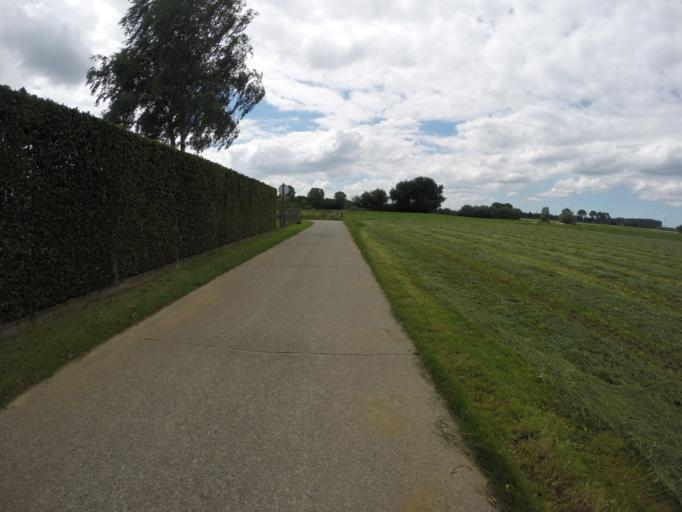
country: BE
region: Flanders
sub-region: Provincie Oost-Vlaanderen
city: Aalter
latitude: 51.1056
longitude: 3.4837
